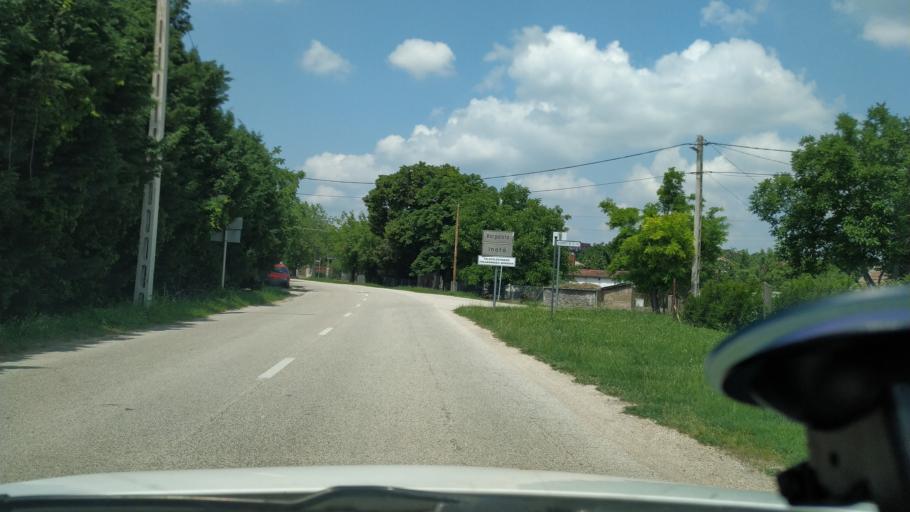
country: HU
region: Veszprem
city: Varpalota
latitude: 47.1988
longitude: 18.1822
